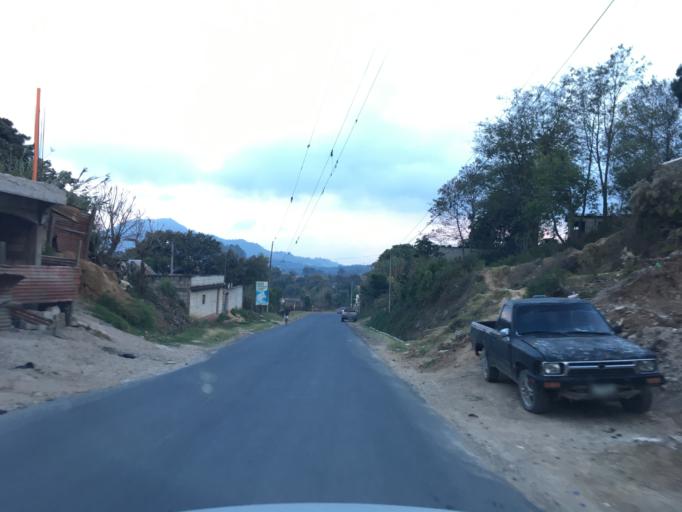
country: GT
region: Chimaltenango
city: Tecpan Guatemala
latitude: 14.7497
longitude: -91.0007
